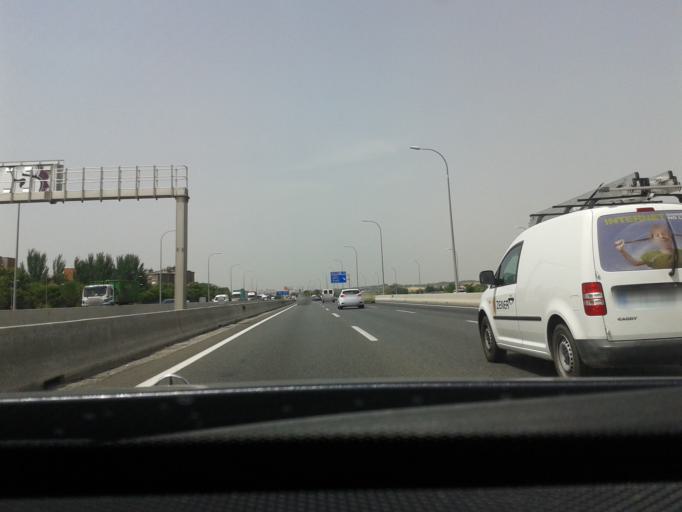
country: ES
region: Madrid
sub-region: Provincia de Madrid
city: Torrejon de Ardoz
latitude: 40.4670
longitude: -3.4614
